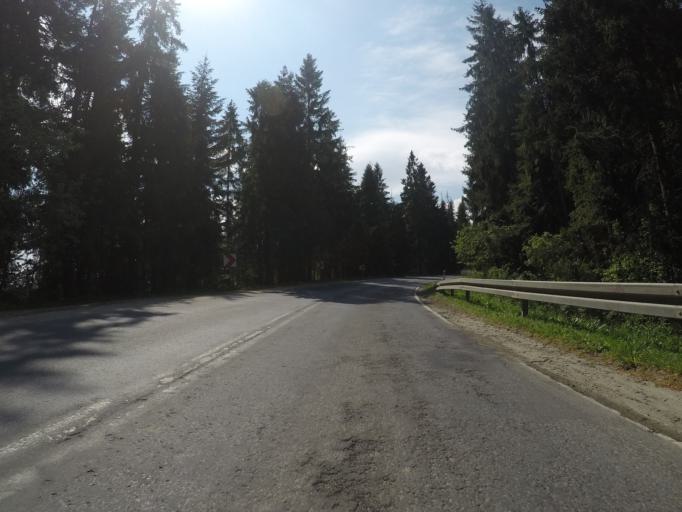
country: PL
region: Lesser Poland Voivodeship
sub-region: Powiat tatrzanski
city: Bukowina Tatrzanska
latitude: 49.3140
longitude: 20.1088
